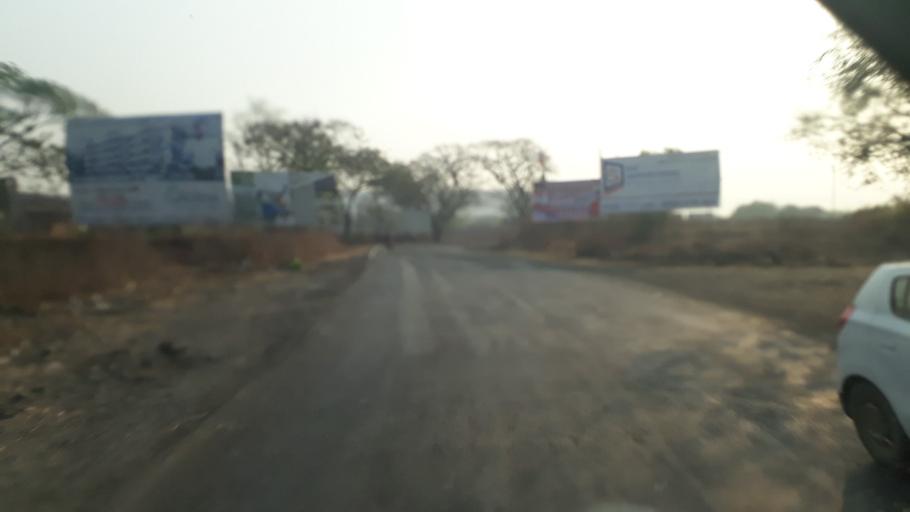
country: IN
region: Maharashtra
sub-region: Raigarh
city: Karjat
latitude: 18.9159
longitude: 73.2887
